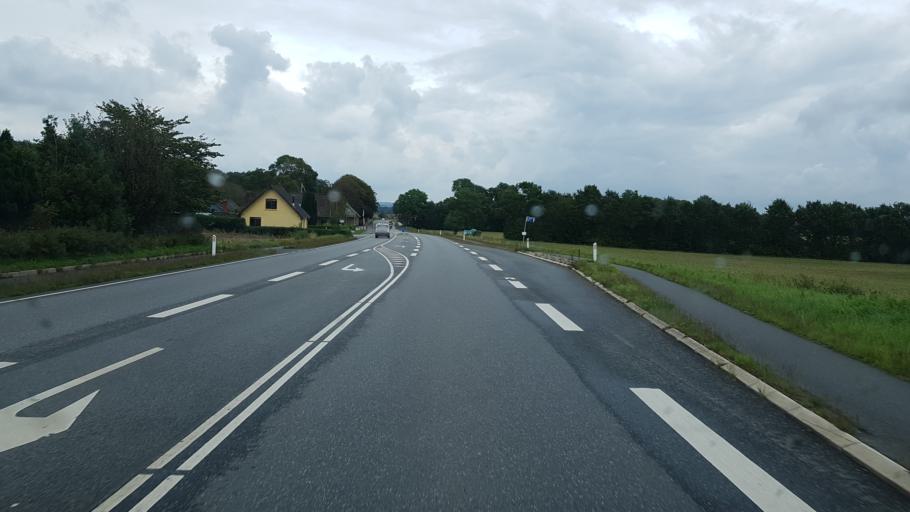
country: DK
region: Central Jutland
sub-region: Horsens Kommune
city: Braedstrup
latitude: 55.9081
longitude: 9.7249
